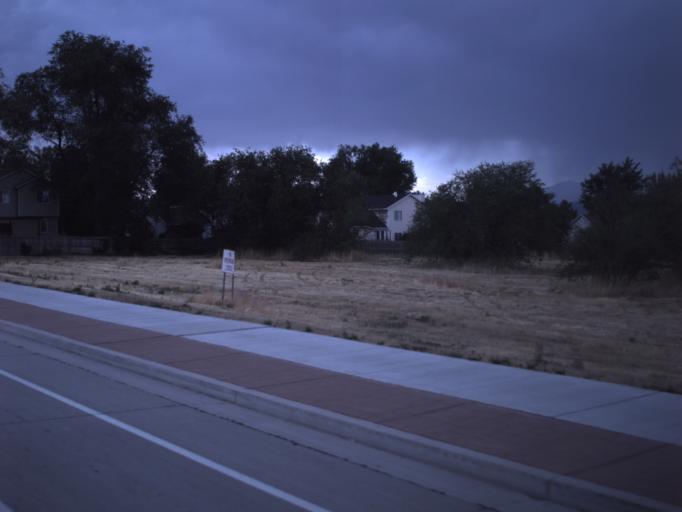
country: US
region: Utah
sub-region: Salt Lake County
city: White City
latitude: 40.5561
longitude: -111.8723
